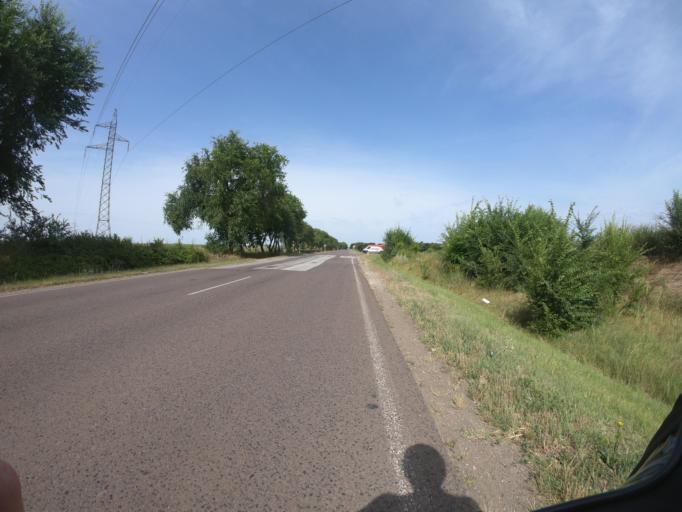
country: HU
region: Jasz-Nagykun-Szolnok
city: Tiszafured
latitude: 47.6006
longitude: 20.8016
